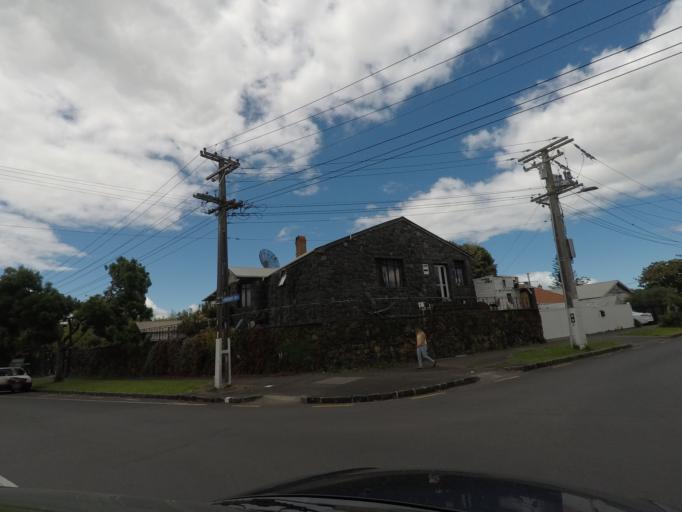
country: NZ
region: Auckland
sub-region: Auckland
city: Auckland
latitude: -36.8788
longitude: 174.7328
